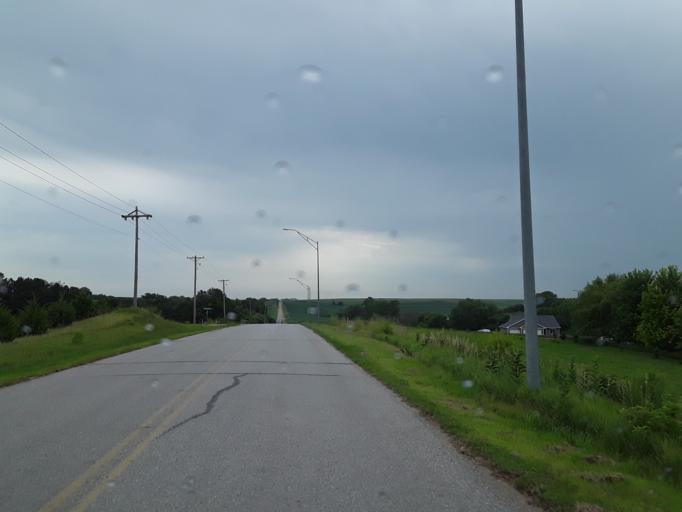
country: US
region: Nebraska
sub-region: Washington County
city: Blair
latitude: 41.5091
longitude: -96.1571
